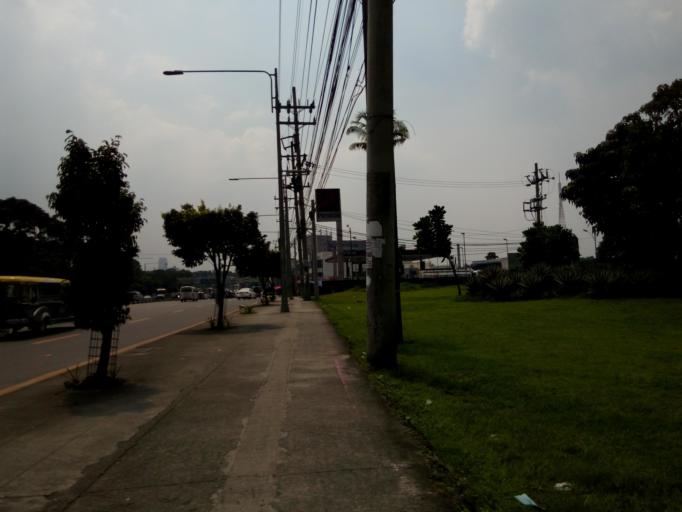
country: PH
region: Metro Manila
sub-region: Quezon City
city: Quezon City
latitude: 14.6553
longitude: 121.0545
